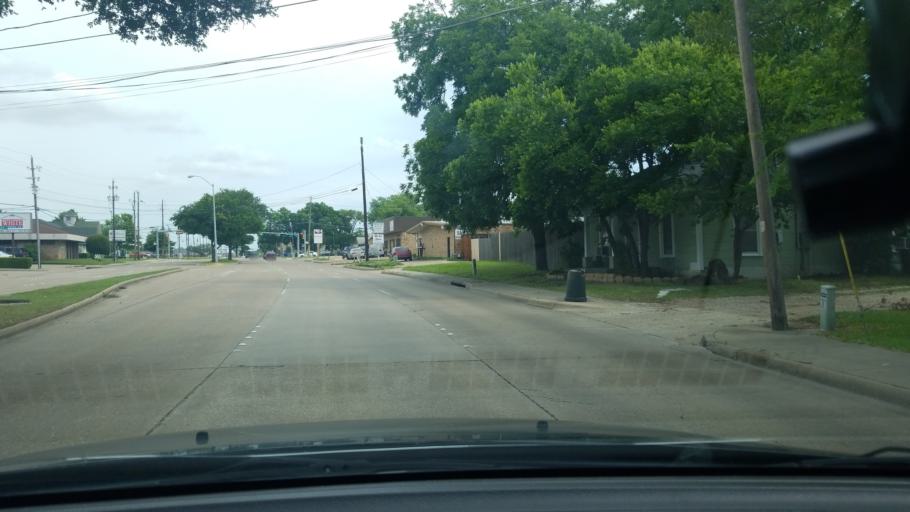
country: US
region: Texas
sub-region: Dallas County
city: Mesquite
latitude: 32.7598
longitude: -96.5972
